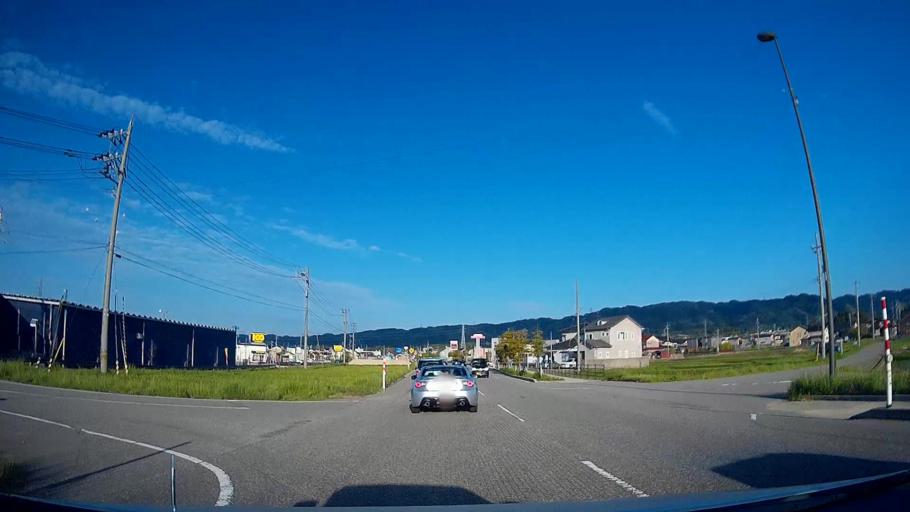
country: JP
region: Ishikawa
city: Nanao
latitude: 37.0324
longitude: 136.9620
